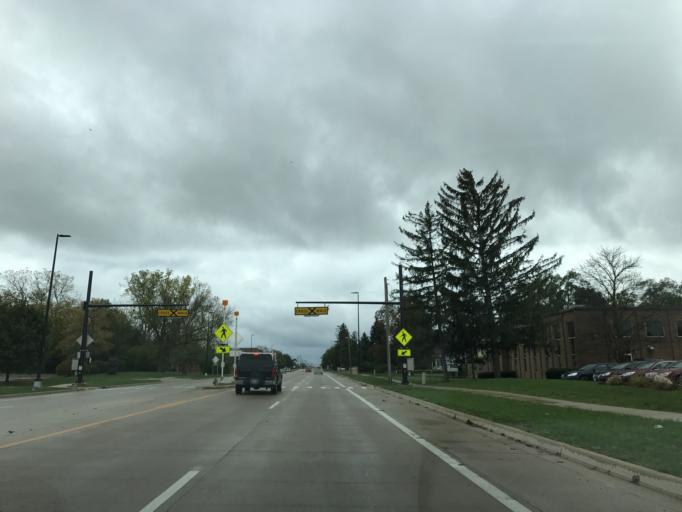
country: US
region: Michigan
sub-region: Washtenaw County
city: Ann Arbor
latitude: 42.2517
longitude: -83.6808
